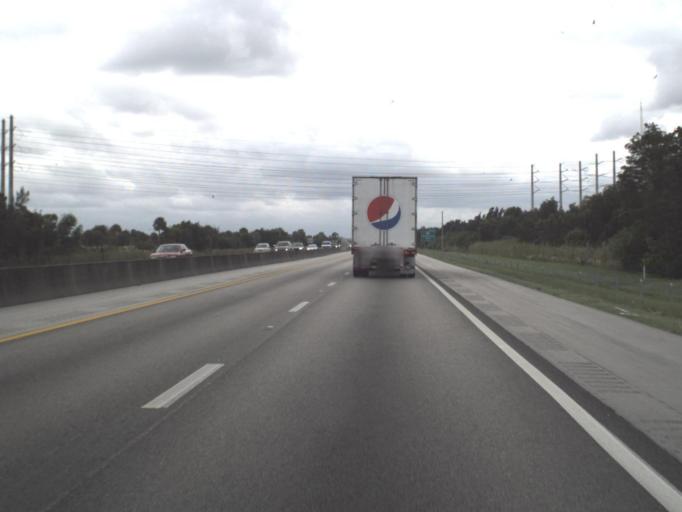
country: US
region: Florida
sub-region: Palm Beach County
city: Schall Circle
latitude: 26.7473
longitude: -80.1346
